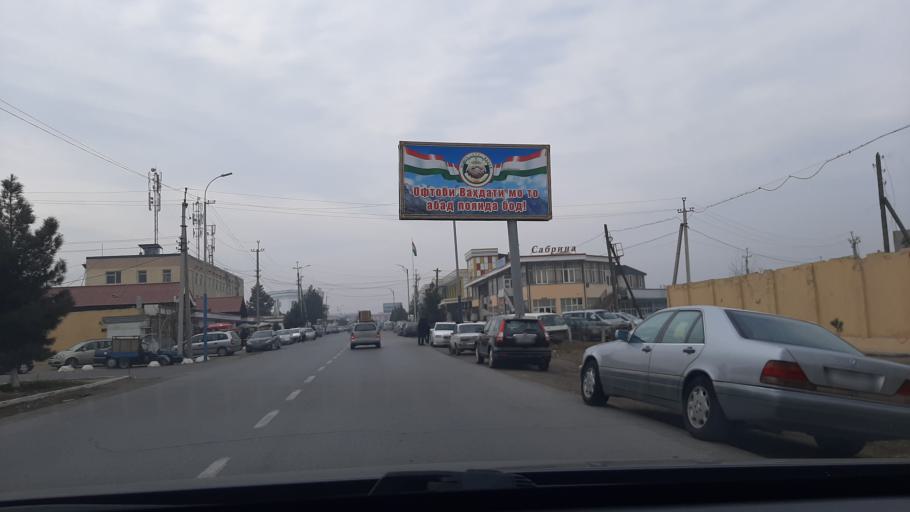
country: TJ
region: Viloyati Sughd
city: Chkalov
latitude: 40.2462
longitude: 69.7043
